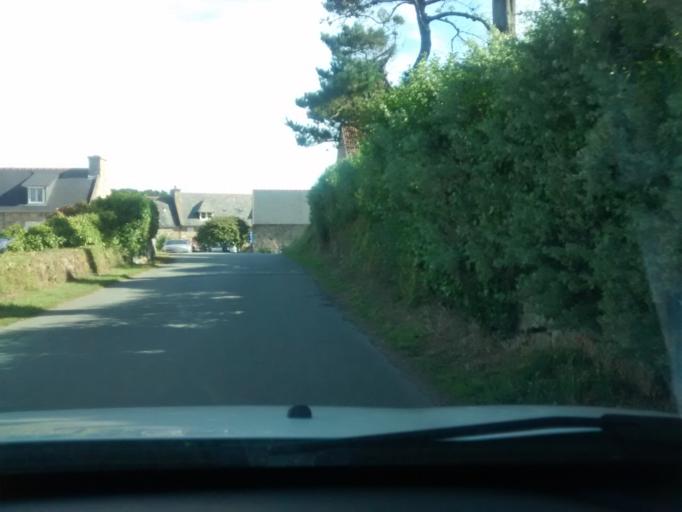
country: FR
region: Brittany
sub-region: Departement des Cotes-d'Armor
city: Plougrescant
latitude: 48.8652
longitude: -3.2250
